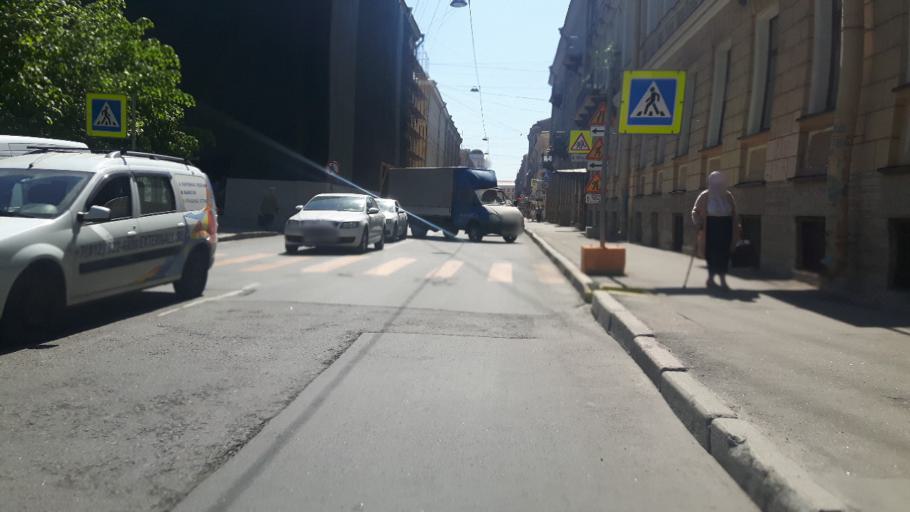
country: RU
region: St.-Petersburg
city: Saint Petersburg
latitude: 59.9302
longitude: 30.3041
